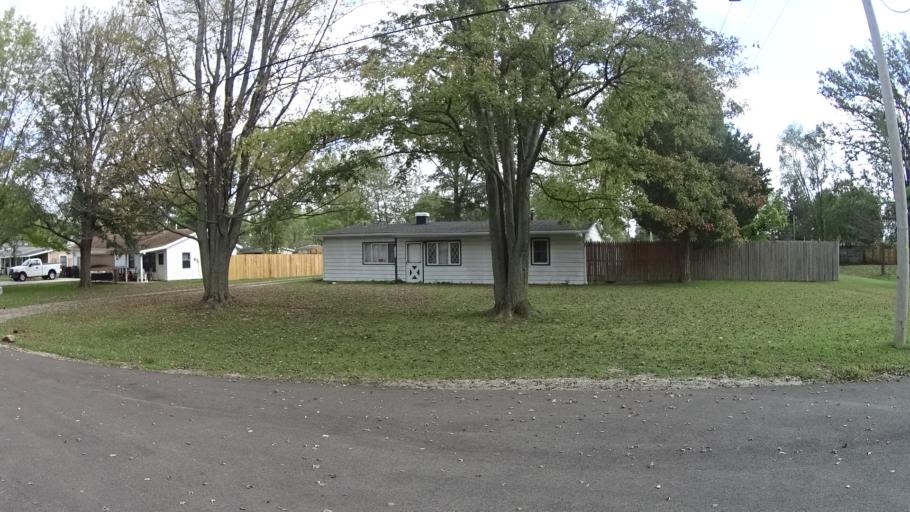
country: US
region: Ohio
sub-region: Lorain County
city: Eaton Estates
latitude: 41.3072
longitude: -82.0043
